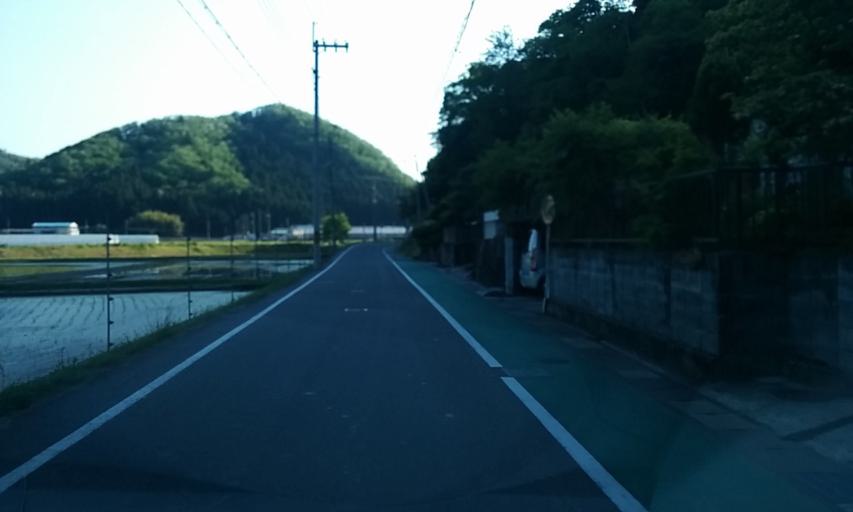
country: JP
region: Kyoto
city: Kameoka
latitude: 35.1441
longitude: 135.4255
